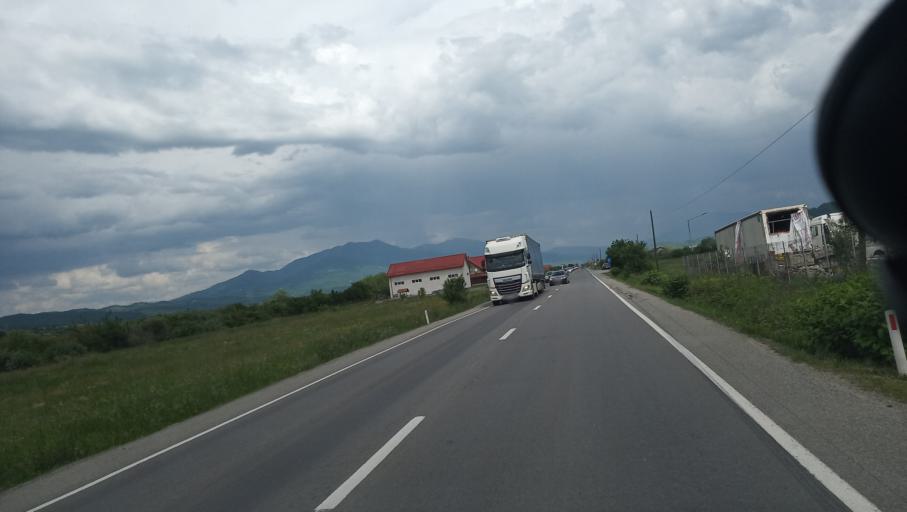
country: RO
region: Bistrita-Nasaud
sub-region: Comuna Livezile
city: Livezile
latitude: 47.1882
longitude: 24.6035
